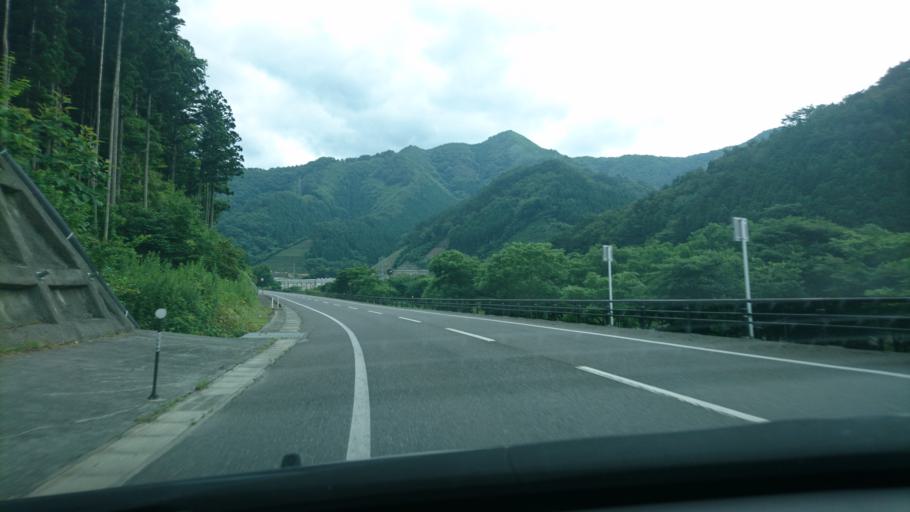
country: JP
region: Iwate
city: Kamaishi
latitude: 39.3003
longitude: 141.8797
